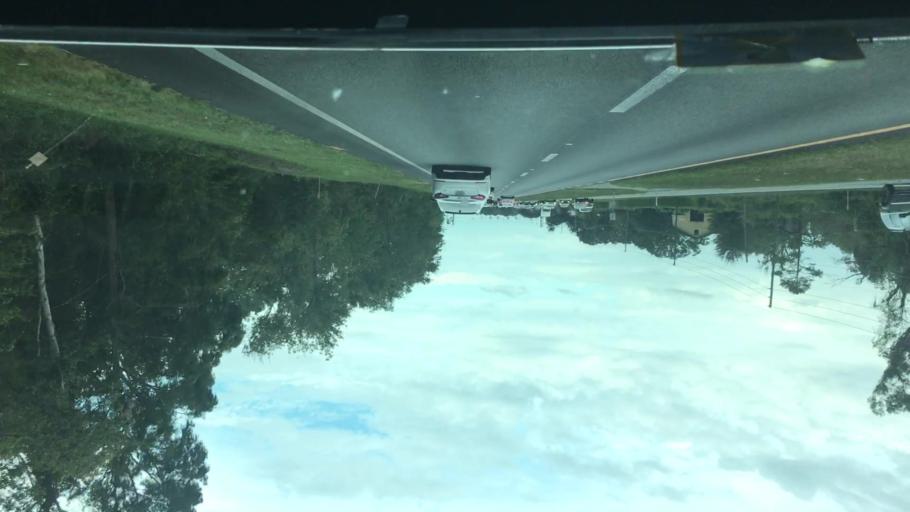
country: US
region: Florida
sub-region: Orange County
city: Bithlo
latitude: 28.5546
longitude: -81.1102
